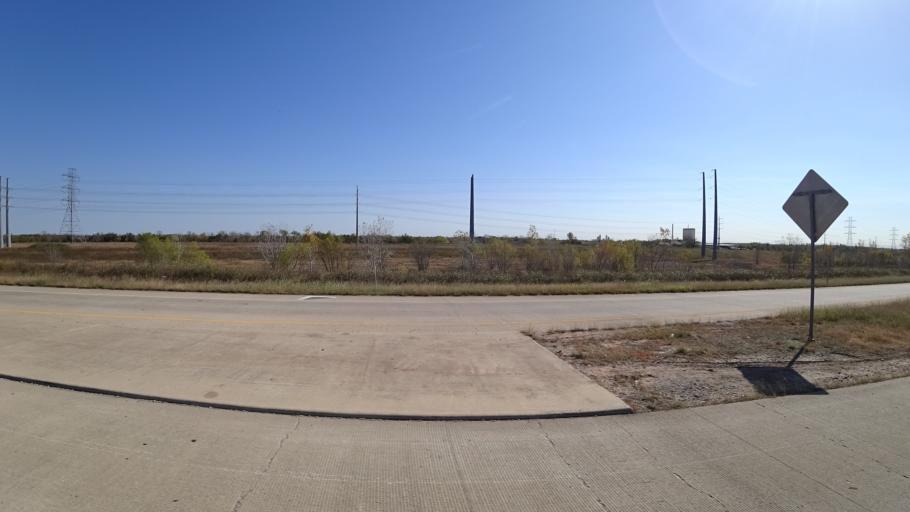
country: US
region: Texas
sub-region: Travis County
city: Hornsby Bend
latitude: 30.2356
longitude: -97.6161
